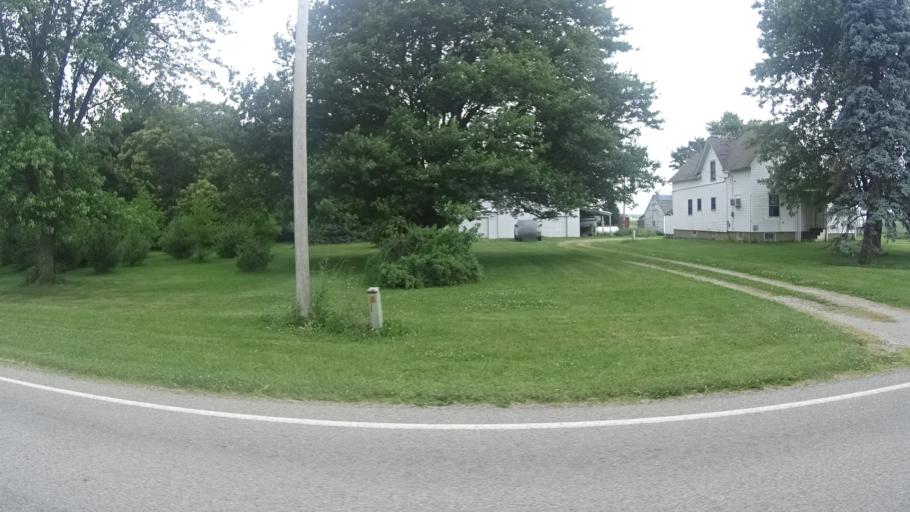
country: US
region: Ohio
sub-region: Huron County
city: Monroeville
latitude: 41.3232
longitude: -82.6838
